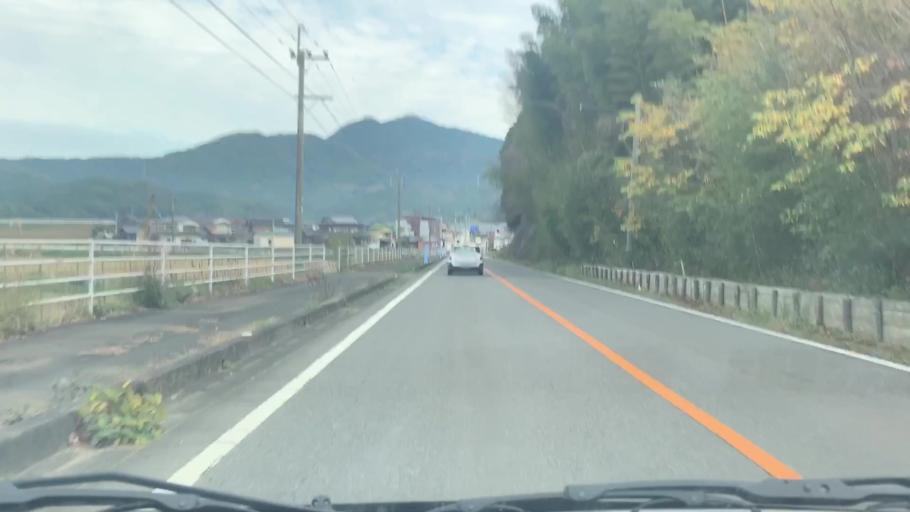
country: JP
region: Saga Prefecture
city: Takeocho-takeo
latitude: 33.2555
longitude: 129.9729
